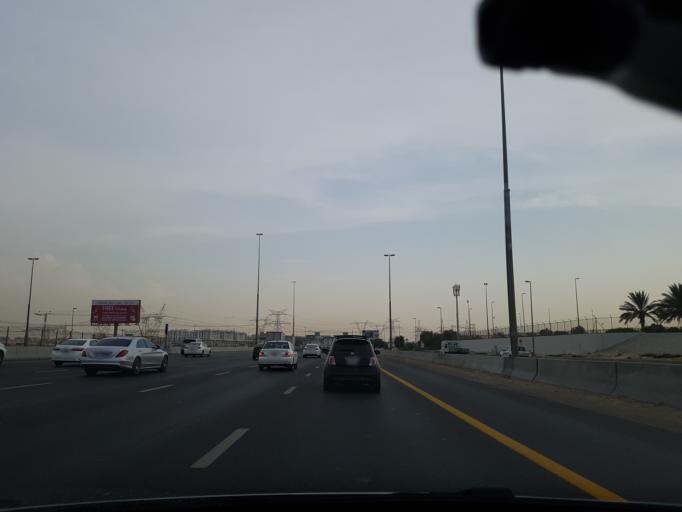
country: AE
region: Ash Shariqah
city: Sharjah
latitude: 25.2286
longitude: 55.4039
